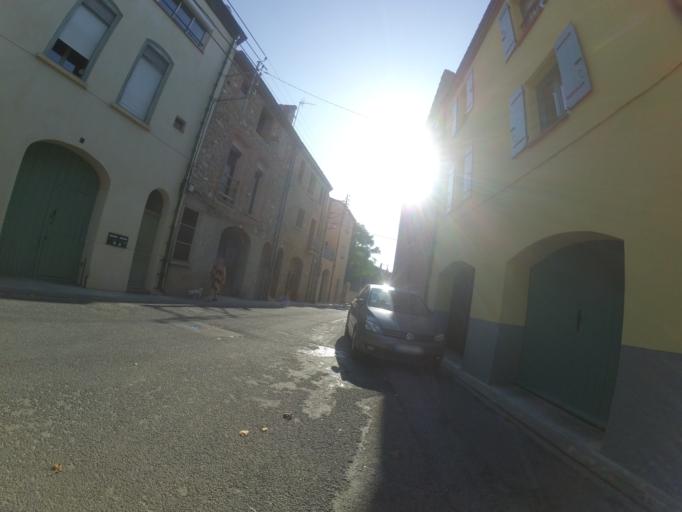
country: FR
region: Languedoc-Roussillon
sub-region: Departement des Pyrenees-Orientales
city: Baixas
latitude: 42.7516
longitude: 2.8089
